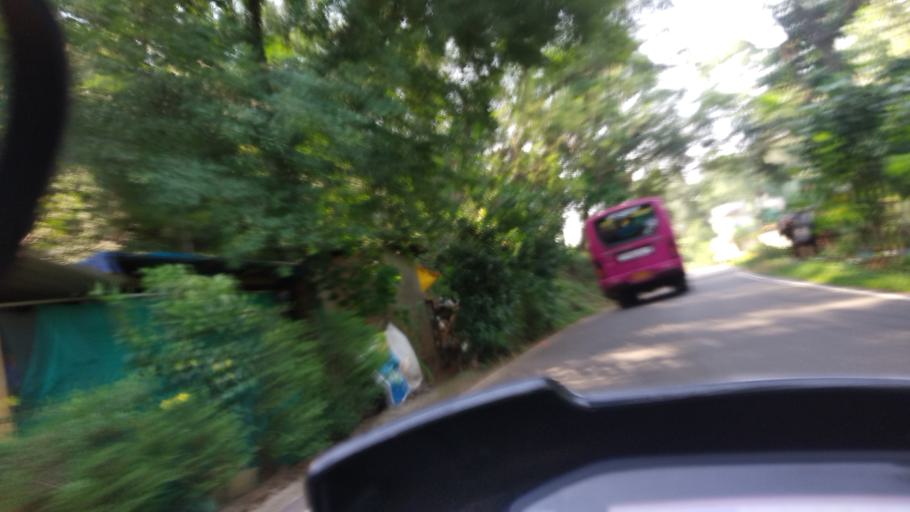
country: IN
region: Kerala
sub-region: Ernakulam
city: Piravam
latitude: 9.8171
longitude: 76.5573
